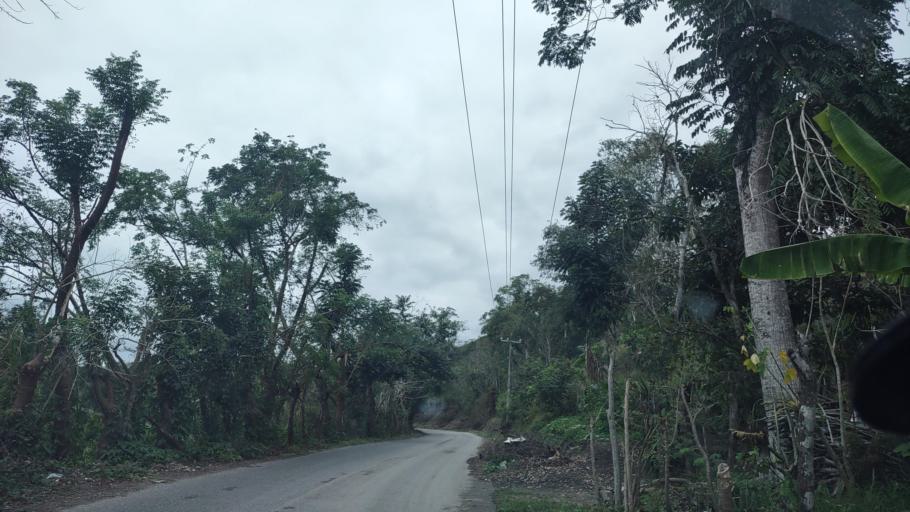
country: MX
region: Veracruz
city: Papantla de Olarte
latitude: 20.4433
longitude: -97.2879
